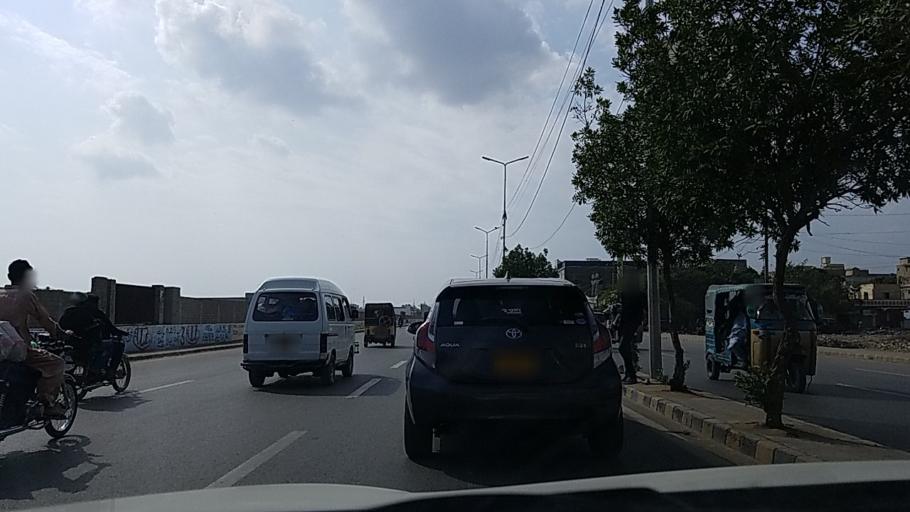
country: PK
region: Sindh
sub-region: Karachi District
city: Karachi
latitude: 24.8213
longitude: 67.1290
